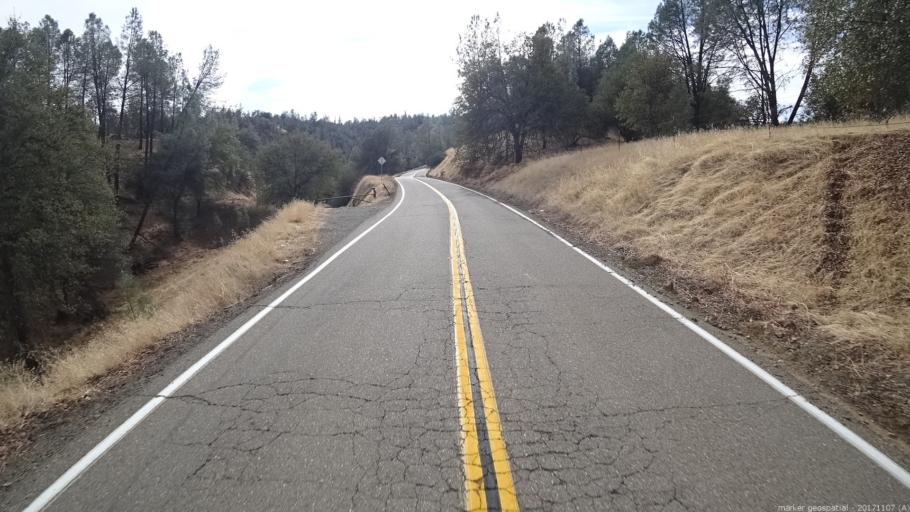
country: US
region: California
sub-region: Shasta County
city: Shasta
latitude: 40.5127
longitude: -122.5197
